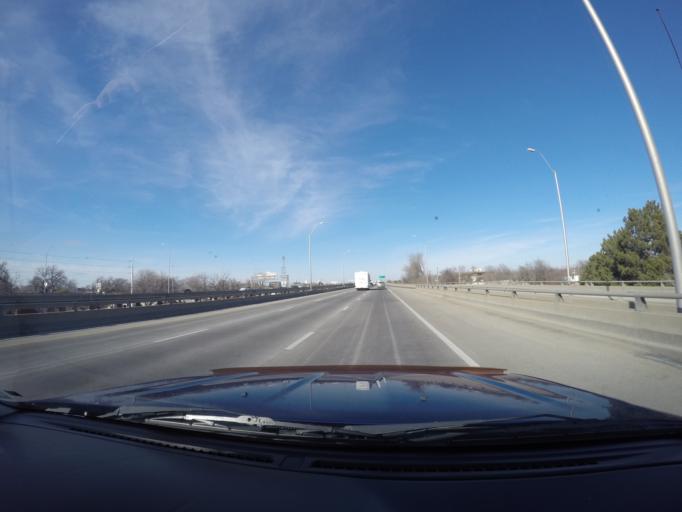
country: US
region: Kansas
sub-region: Sedgwick County
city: Wichita
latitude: 37.6914
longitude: -97.3144
